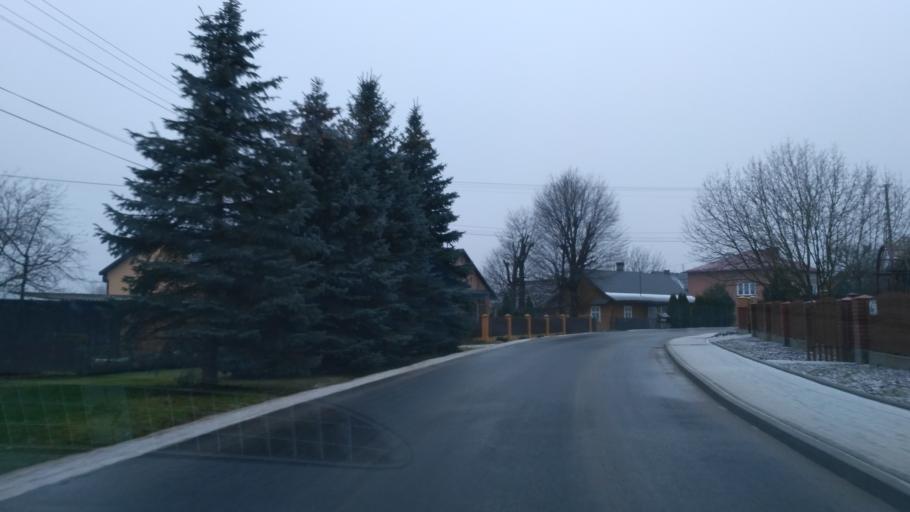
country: PL
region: Subcarpathian Voivodeship
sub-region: Powiat przeworski
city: Gac
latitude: 50.0246
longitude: 22.3895
